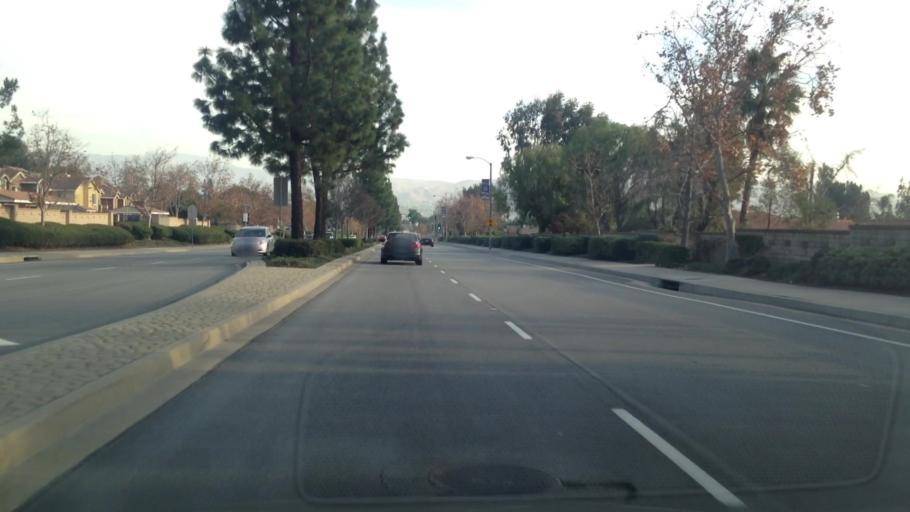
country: US
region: California
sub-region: Orange County
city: Yorba Linda
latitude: 33.8859
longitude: -117.7578
